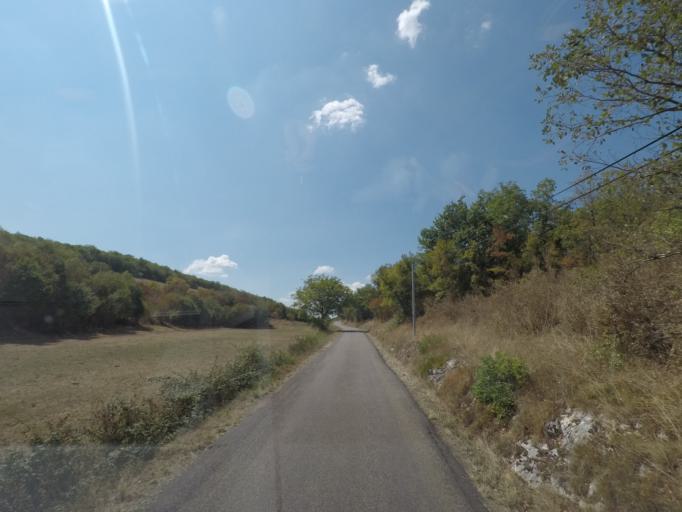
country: FR
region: Midi-Pyrenees
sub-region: Departement du Lot
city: Lalbenque
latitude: 44.5167
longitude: 1.6398
